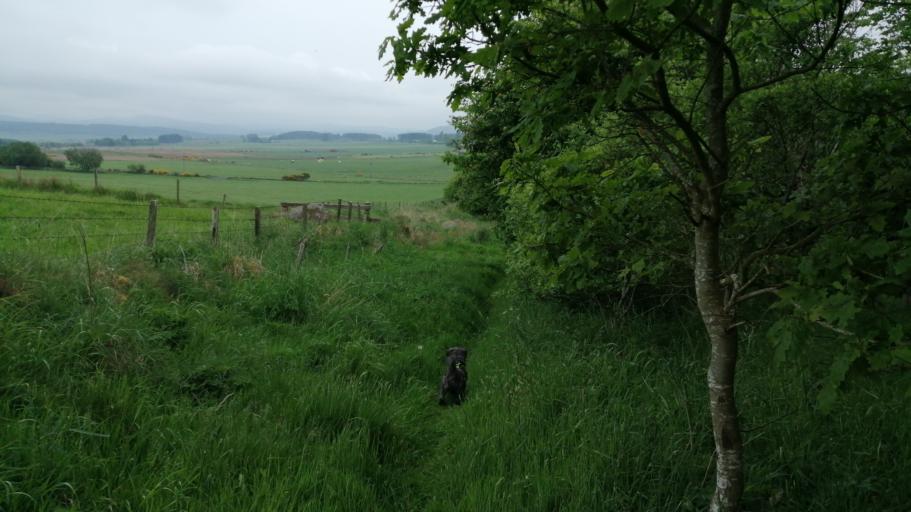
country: GB
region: Scotland
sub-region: Moray
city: Cullen
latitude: 57.5778
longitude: -2.7873
